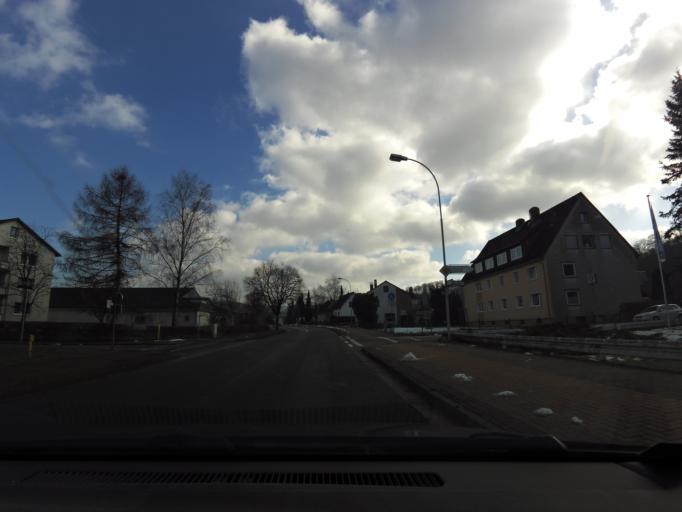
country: DE
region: Lower Saxony
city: Bad Lauterberg im Harz
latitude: 51.6210
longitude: 10.4384
